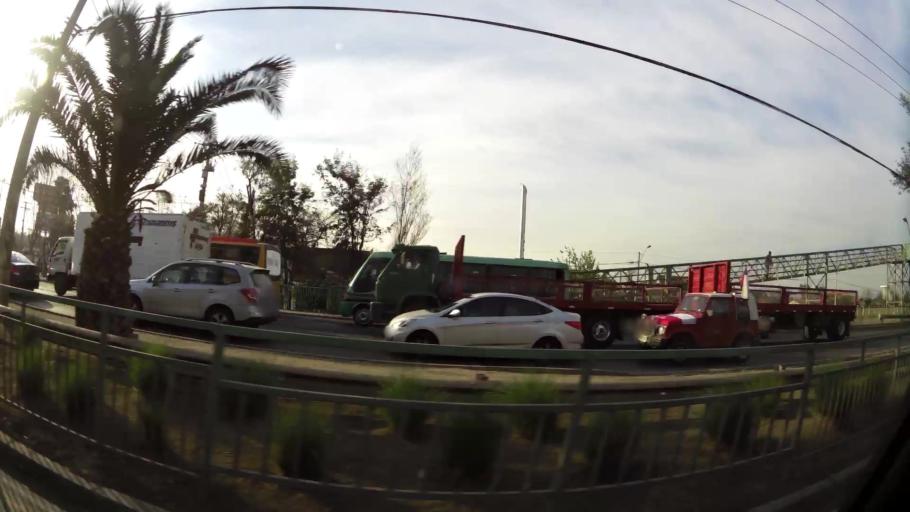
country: CL
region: Santiago Metropolitan
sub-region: Provincia de Talagante
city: Penaflor
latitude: -33.5543
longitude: -70.7963
